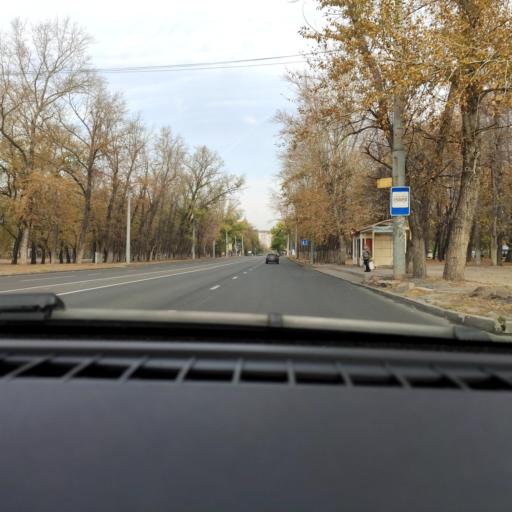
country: RU
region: Voronezj
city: Maslovka
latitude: 51.6073
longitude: 39.2446
